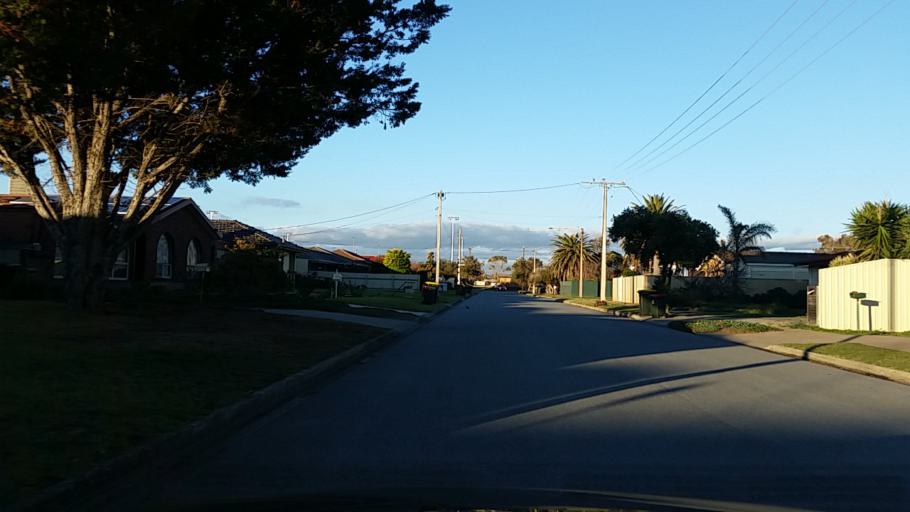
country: AU
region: South Australia
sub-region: Onkaparinga
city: Seaford
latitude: -35.1744
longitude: 138.4682
